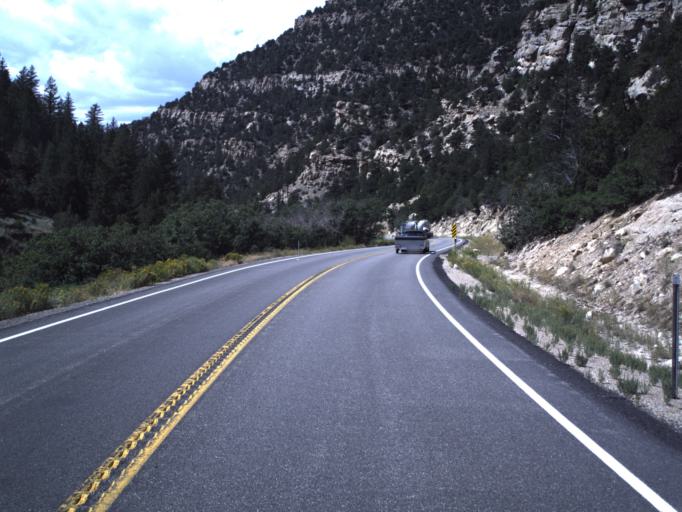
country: US
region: Utah
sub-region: Carbon County
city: Helper
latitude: 39.7583
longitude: -110.8186
